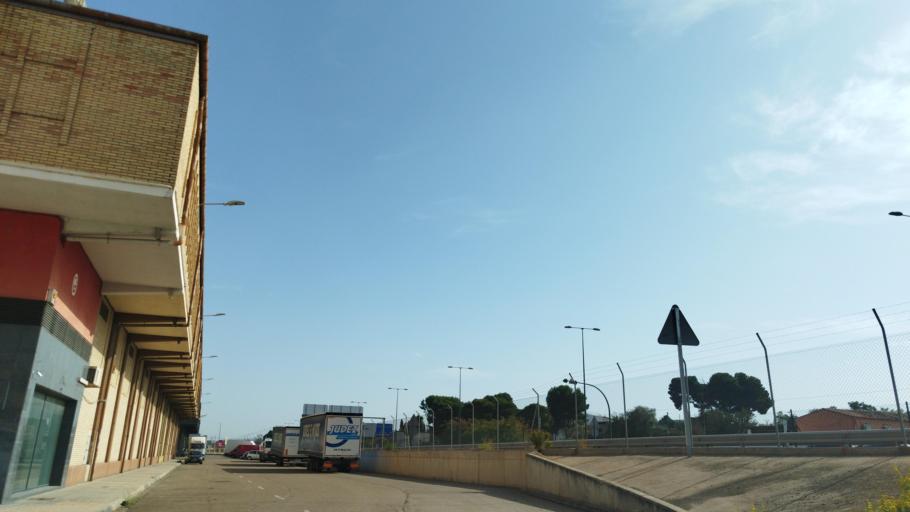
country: ES
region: Aragon
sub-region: Provincia de Zaragoza
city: Oliver-Valdefierro, Oliver, Valdefierro
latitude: 41.6724
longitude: -0.9487
